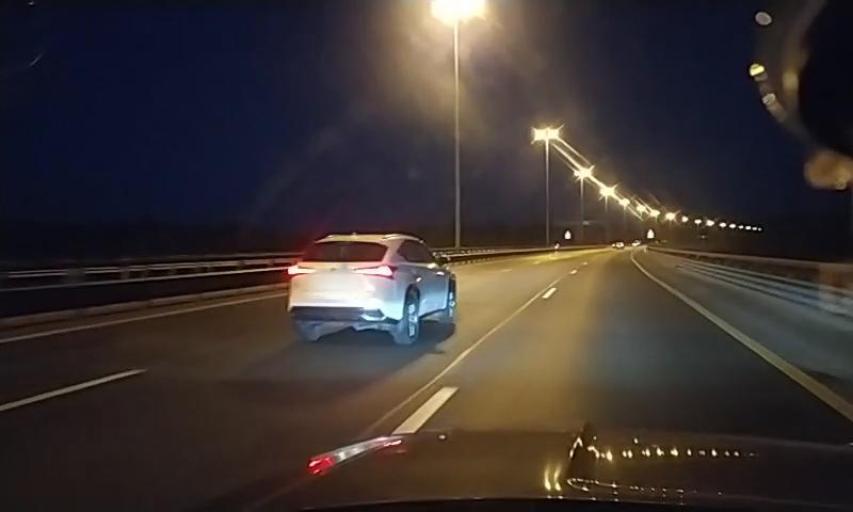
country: RU
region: St.-Petersburg
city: Pesochnyy
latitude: 60.0850
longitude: 30.1053
